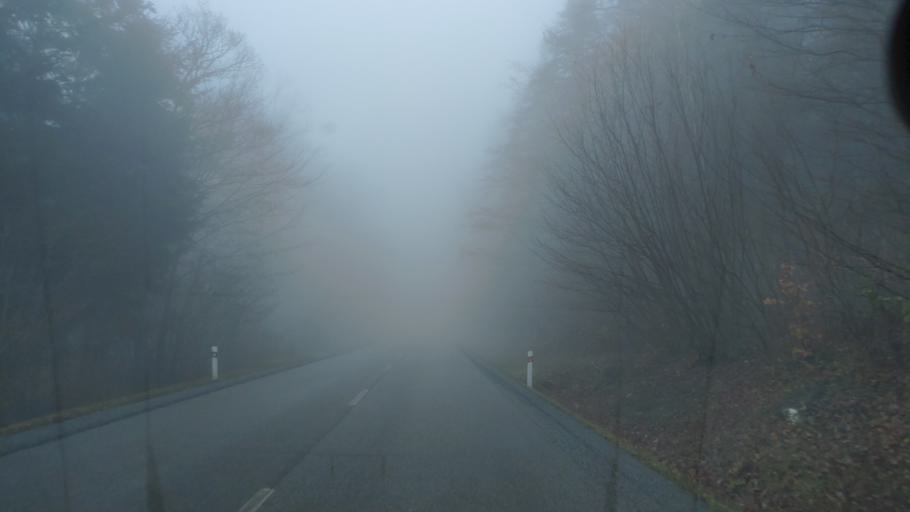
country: SK
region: Banskobystricky
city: Revuca
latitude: 48.6466
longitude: 20.2889
